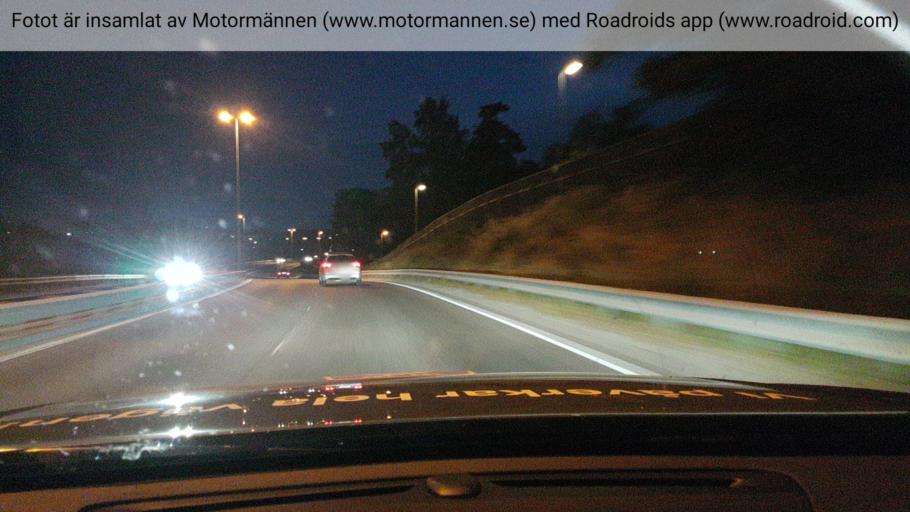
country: SE
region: Stockholm
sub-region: Huddinge Kommun
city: Huddinge
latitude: 59.2426
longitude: 17.9874
